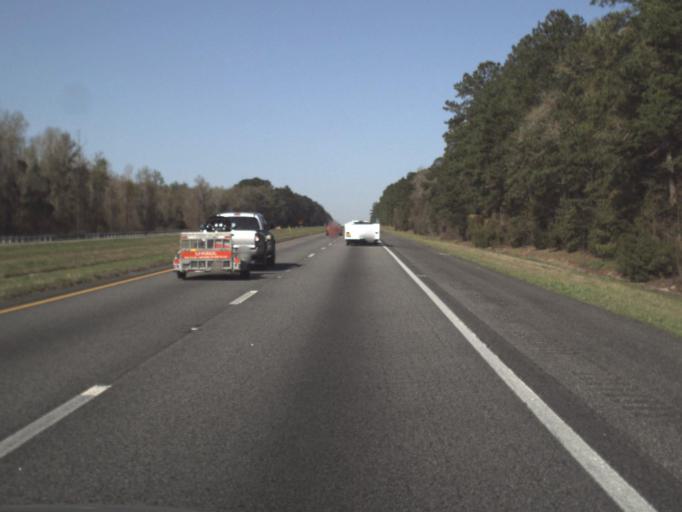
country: US
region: Florida
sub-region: Jefferson County
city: Monticello
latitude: 30.4733
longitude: -83.8588
